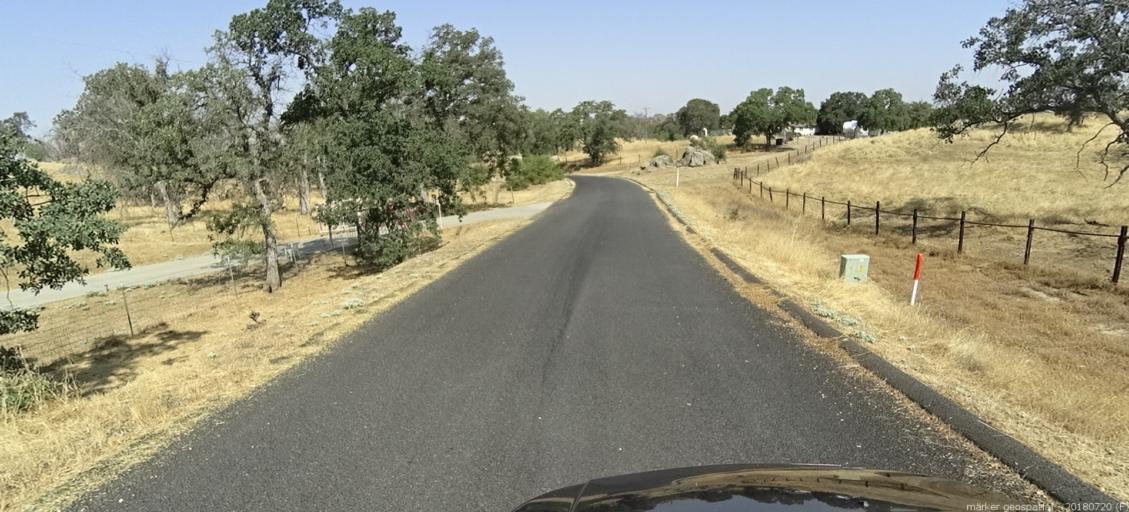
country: US
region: California
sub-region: Madera County
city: Yosemite Lakes
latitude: 37.2335
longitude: -119.9139
